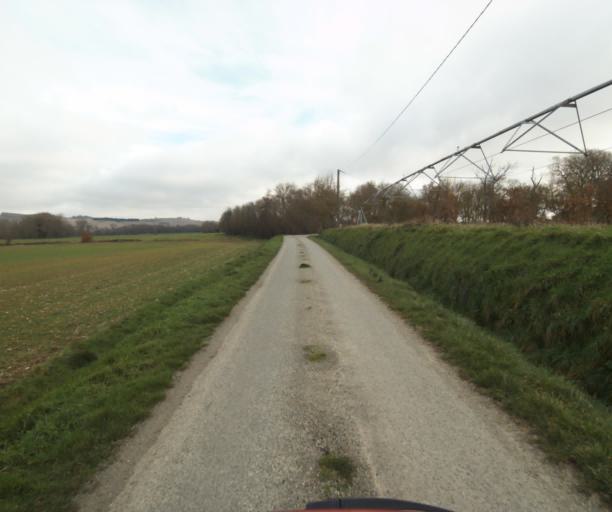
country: FR
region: Midi-Pyrenees
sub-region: Departement de l'Ariege
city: Mazeres
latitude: 43.2286
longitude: 1.7143
